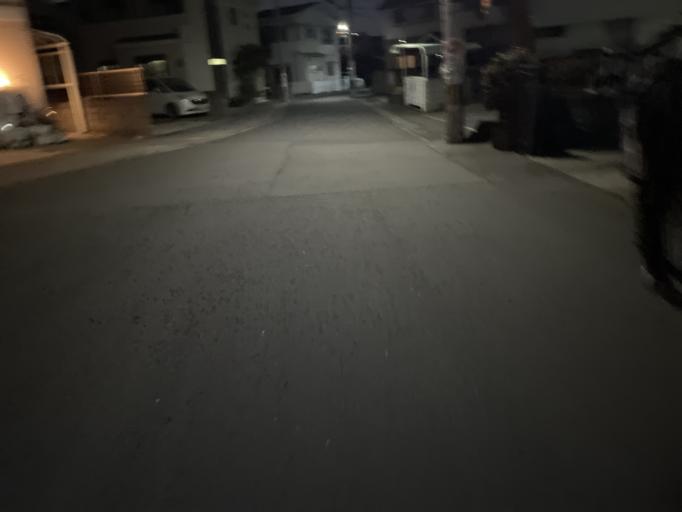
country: JP
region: Osaka
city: Ibaraki
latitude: 34.8071
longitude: 135.5823
